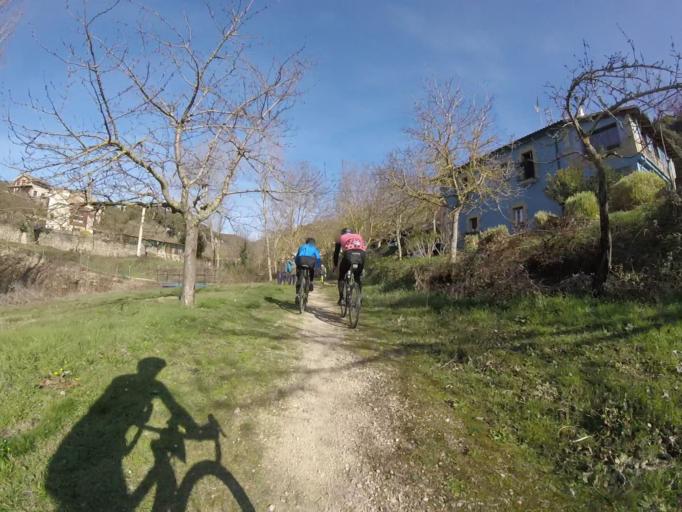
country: ES
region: Navarre
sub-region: Provincia de Navarra
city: Lezaun
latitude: 42.7285
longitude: -2.0212
